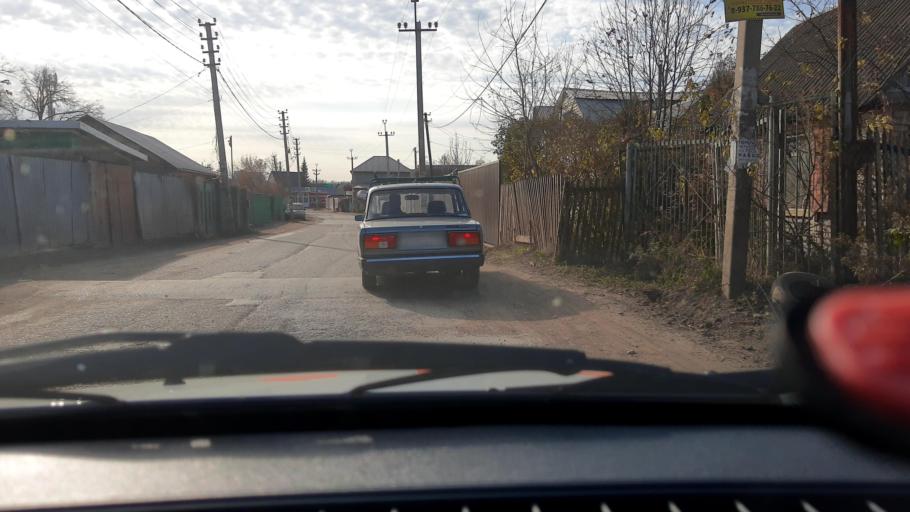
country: RU
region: Bashkortostan
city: Ufa
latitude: 54.6930
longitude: 55.9007
